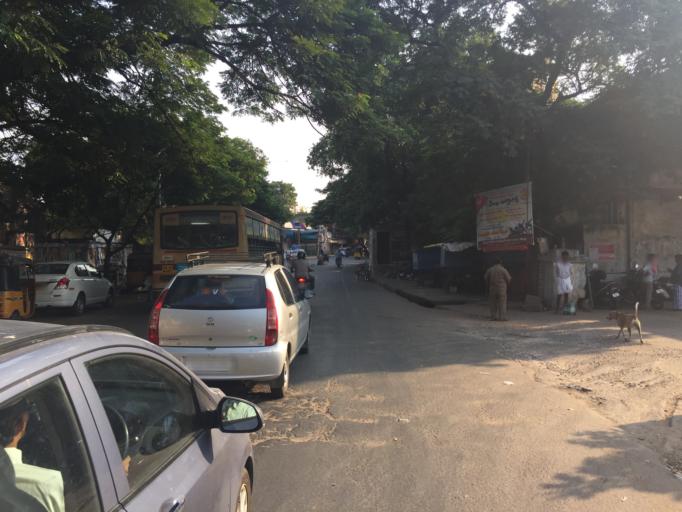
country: IN
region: Tamil Nadu
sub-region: Chennai
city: Gandhi Nagar
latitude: 13.0270
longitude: 80.2661
